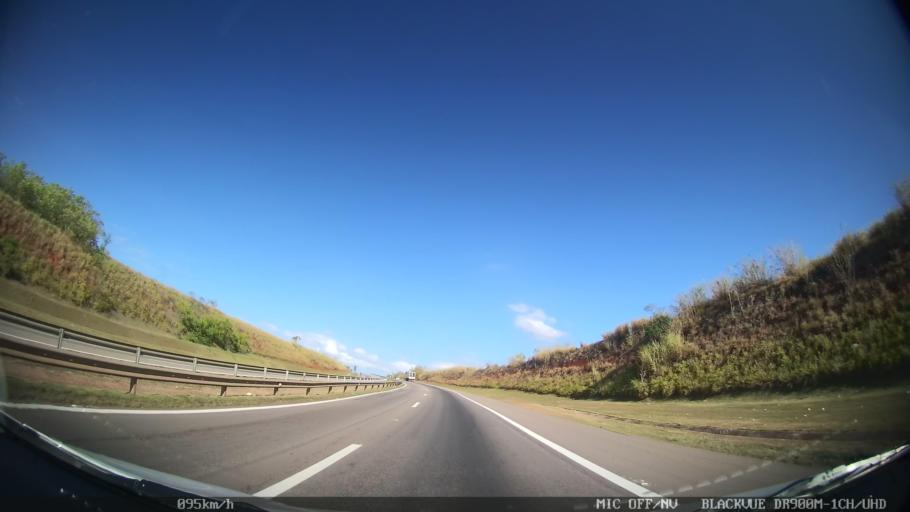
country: BR
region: Sao Paulo
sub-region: Piracicaba
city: Piracicaba
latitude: -22.7106
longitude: -47.6107
